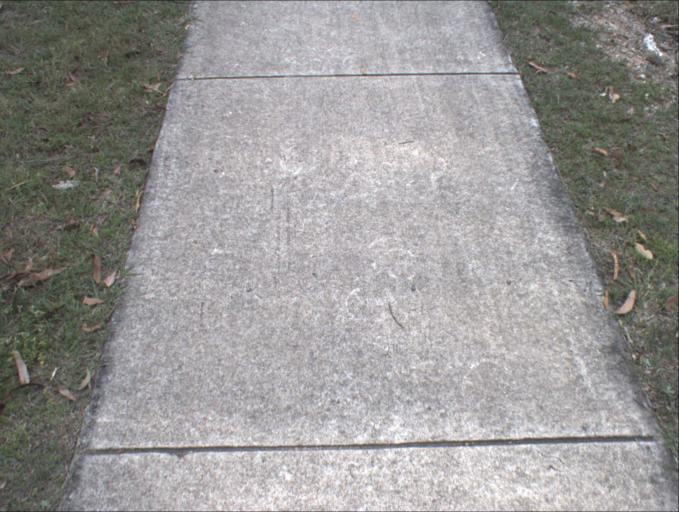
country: AU
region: Queensland
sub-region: Logan
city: Logan Reserve
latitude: -27.7219
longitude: 153.0905
